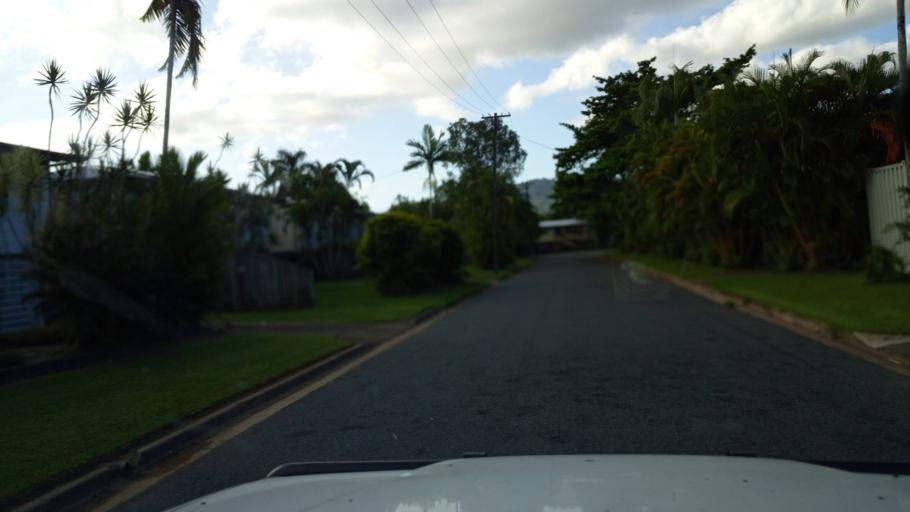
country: AU
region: Queensland
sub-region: Cairns
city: Cairns
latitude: -16.9164
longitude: 145.7563
